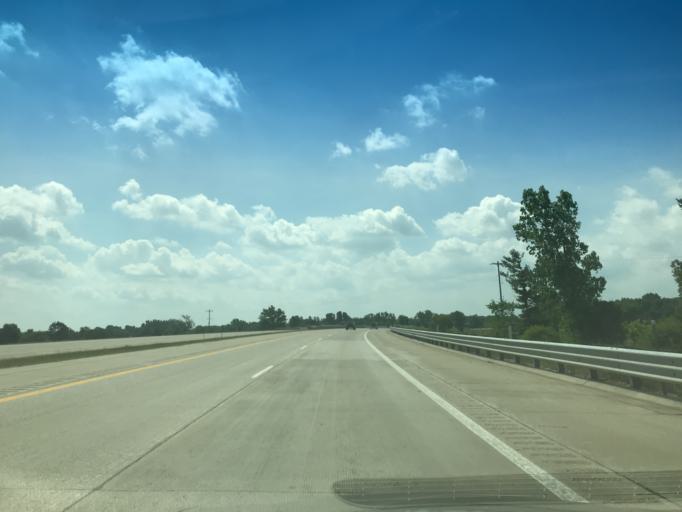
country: US
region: Michigan
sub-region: Clinton County
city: Wacousta
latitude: 42.7875
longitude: -84.6739
